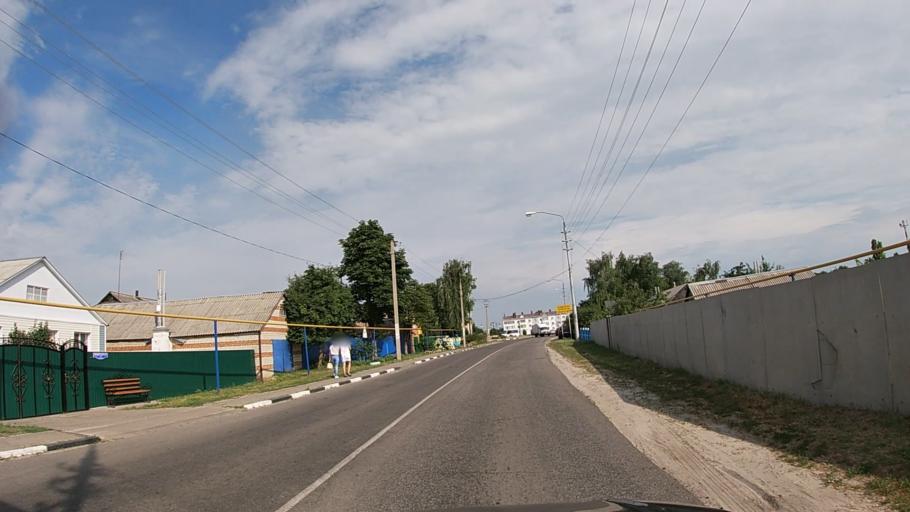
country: RU
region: Belgorod
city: Krasnaya Yaruga
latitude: 50.8007
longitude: 35.6609
